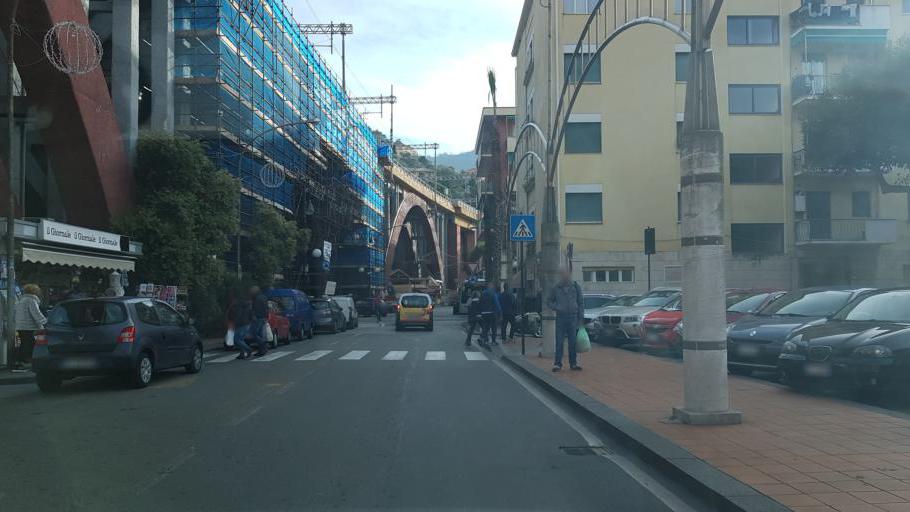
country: IT
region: Liguria
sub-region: Provincia di Genova
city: Recco
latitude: 44.3626
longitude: 9.1438
